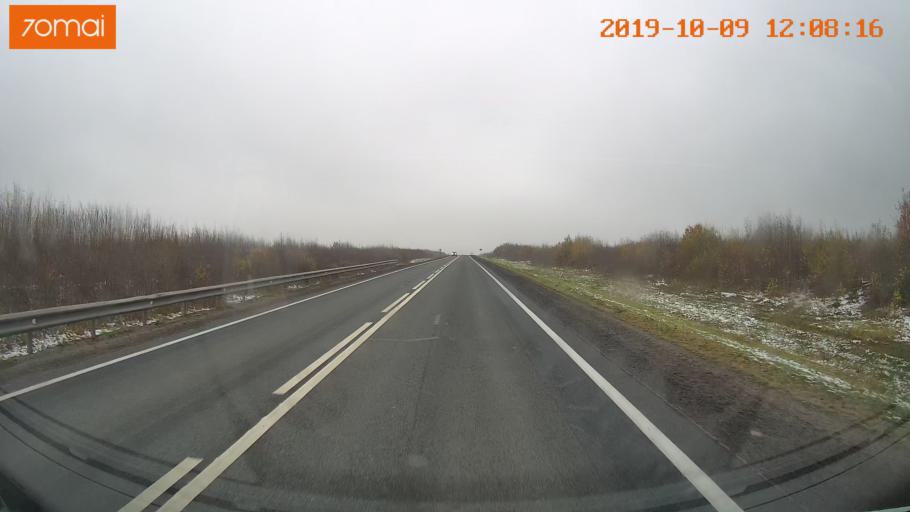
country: RU
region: Jaroslavl
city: Prechistoye
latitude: 58.5889
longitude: 40.3466
